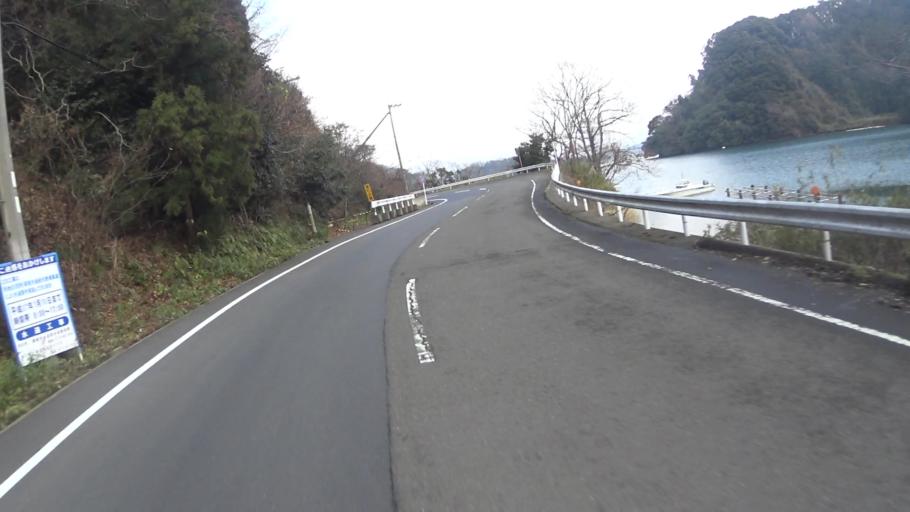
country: JP
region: Kyoto
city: Maizuru
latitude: 35.4768
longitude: 135.3162
